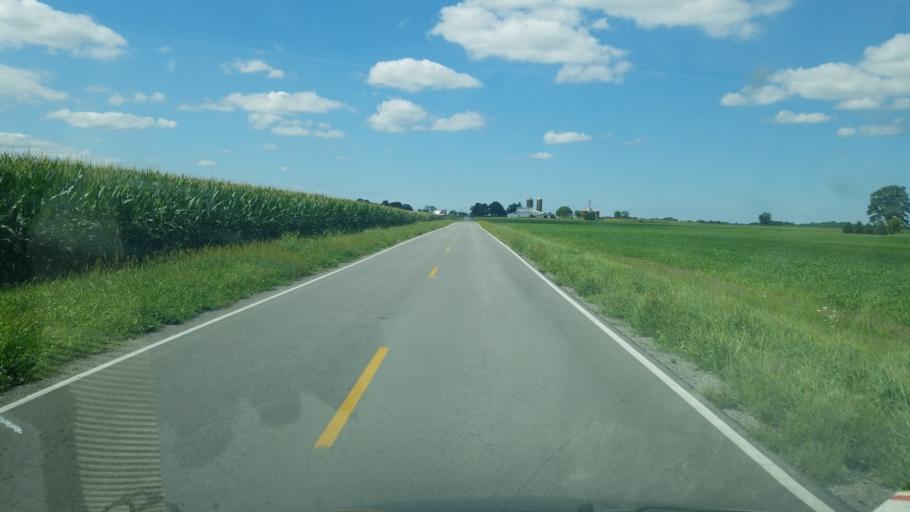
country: US
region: Ohio
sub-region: Fulton County
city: Delta
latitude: 41.6032
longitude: -83.9563
